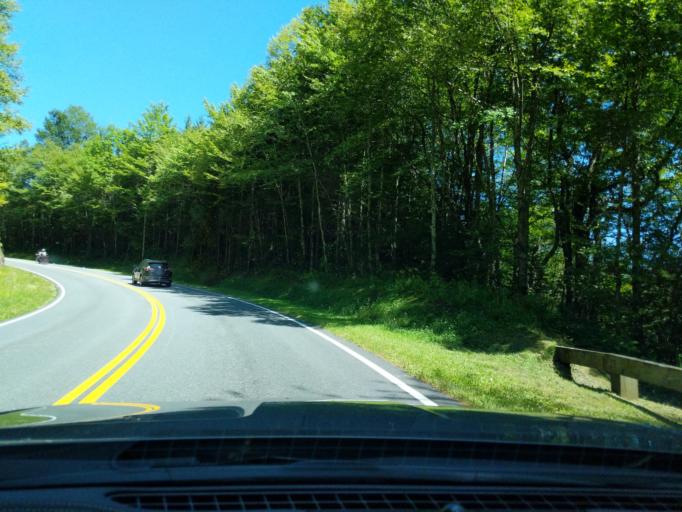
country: US
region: Tennessee
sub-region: Sevier County
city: Gatlinburg
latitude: 35.6080
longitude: -83.4344
